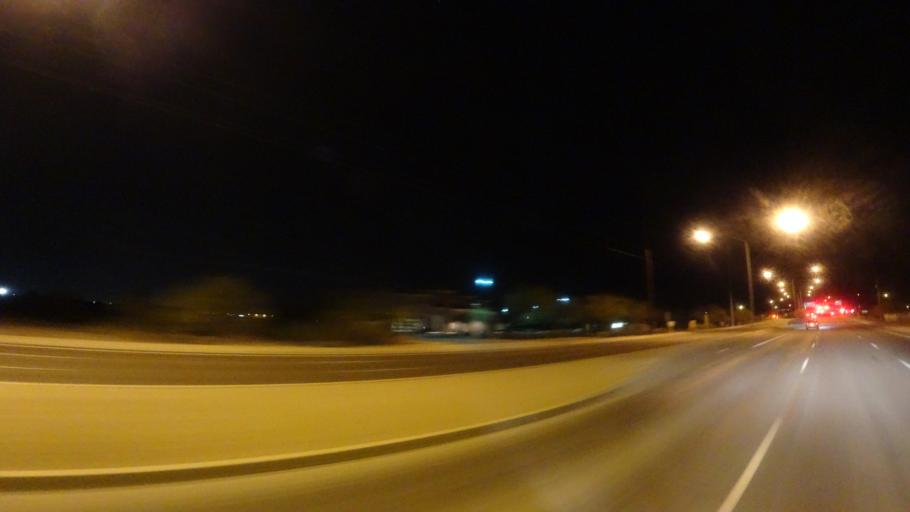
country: US
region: Arizona
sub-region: Maricopa County
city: Mesa
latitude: 33.4778
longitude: -111.7184
